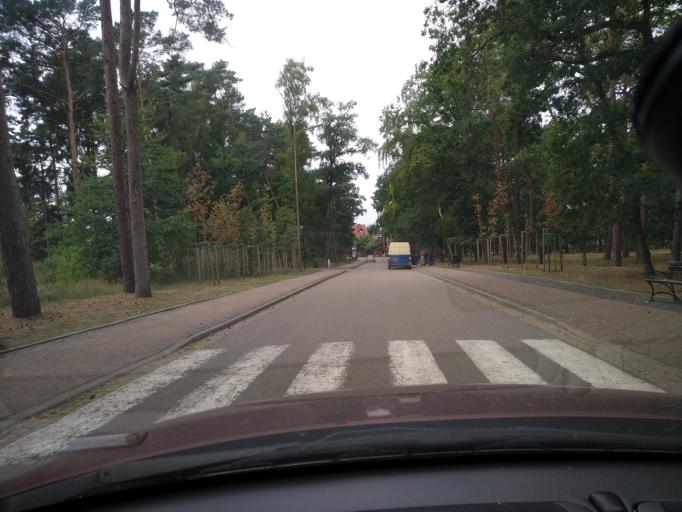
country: PL
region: West Pomeranian Voivodeship
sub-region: Powiat gryficki
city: Pobierowo
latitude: 54.0545
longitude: 14.9344
